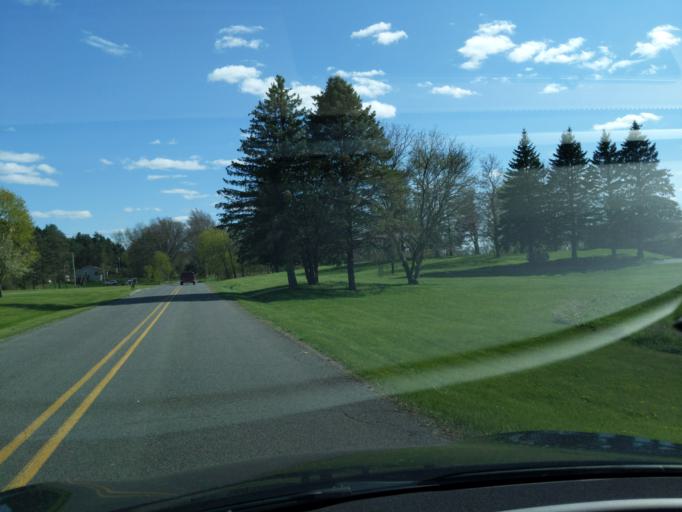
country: US
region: Michigan
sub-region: Jackson County
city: Spring Arbor
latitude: 42.3416
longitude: -84.5220
